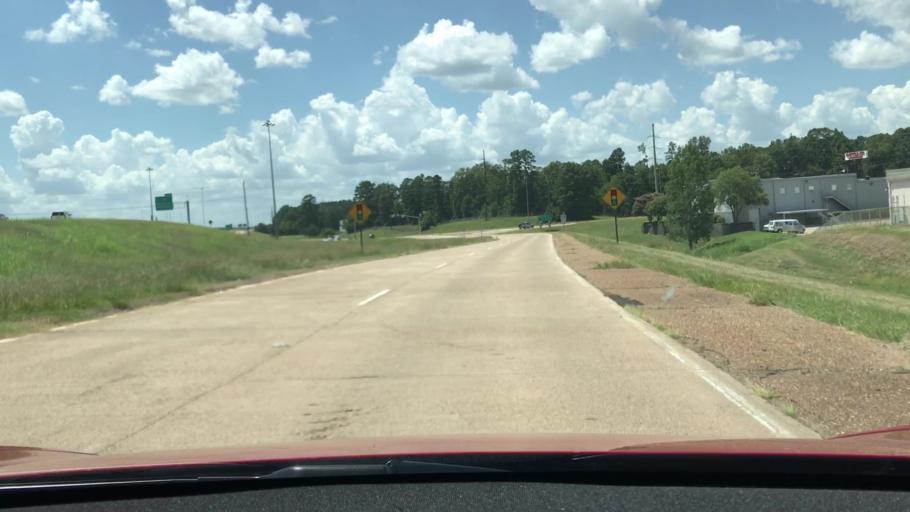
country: US
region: Louisiana
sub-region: Bossier Parish
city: Bossier City
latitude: 32.4154
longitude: -93.7349
